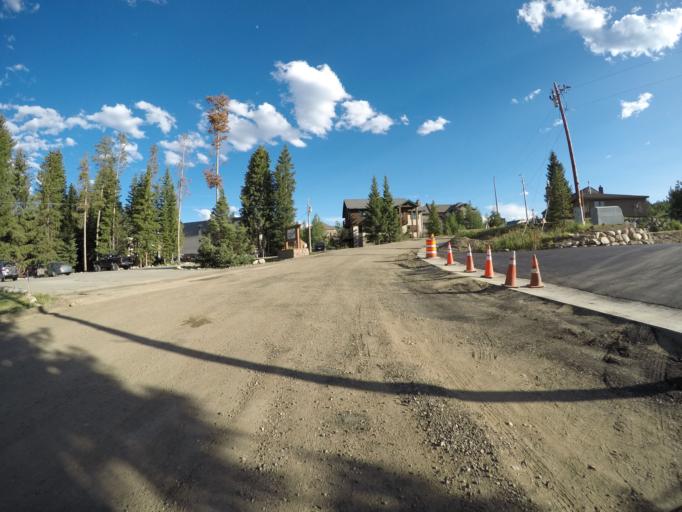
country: US
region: Colorado
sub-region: Grand County
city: Fraser
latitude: 39.9253
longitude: -105.7852
